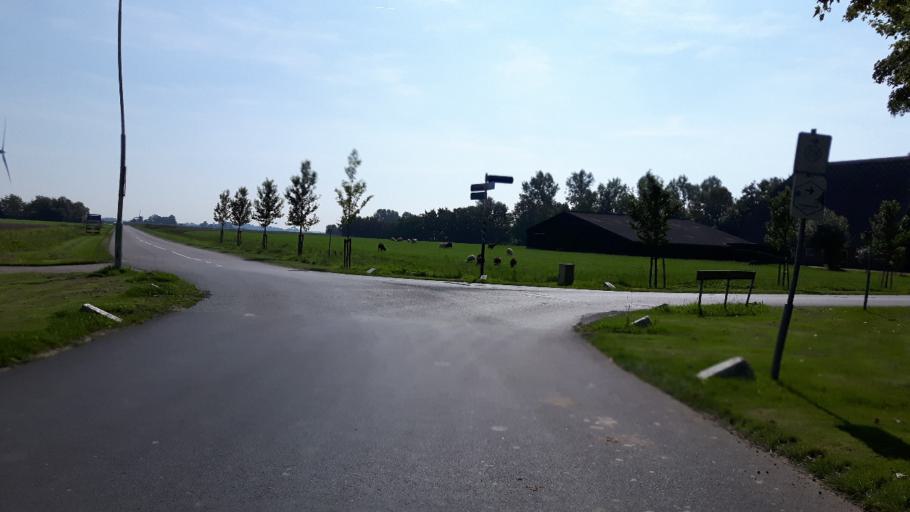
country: NL
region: Friesland
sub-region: Gemeente Ferwerderadiel
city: Marrum
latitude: 53.3287
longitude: 5.8049
